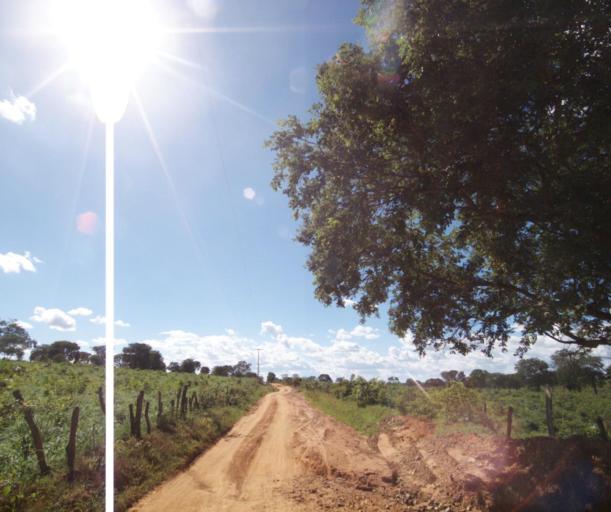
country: BR
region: Bahia
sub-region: Carinhanha
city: Carinhanha
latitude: -14.1822
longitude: -44.5072
